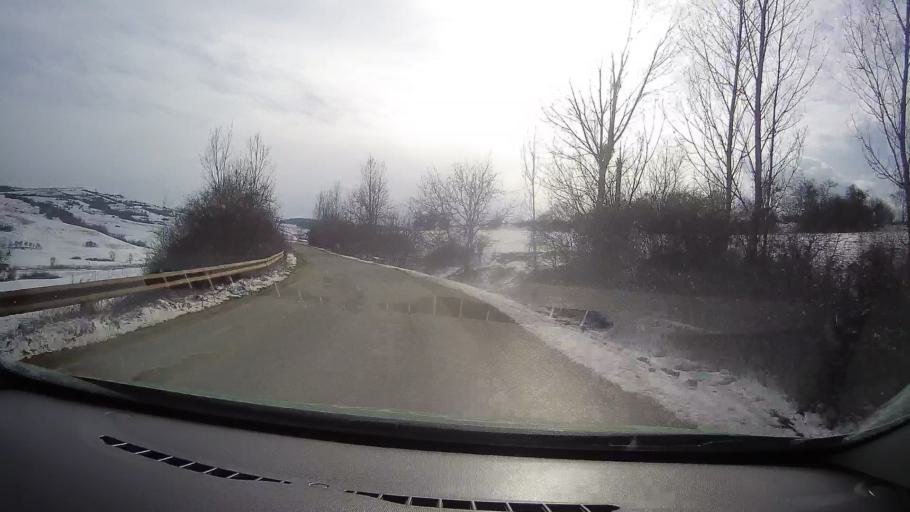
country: RO
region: Sibiu
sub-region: Comuna Bradeni
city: Bradeni
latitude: 46.1051
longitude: 24.8412
